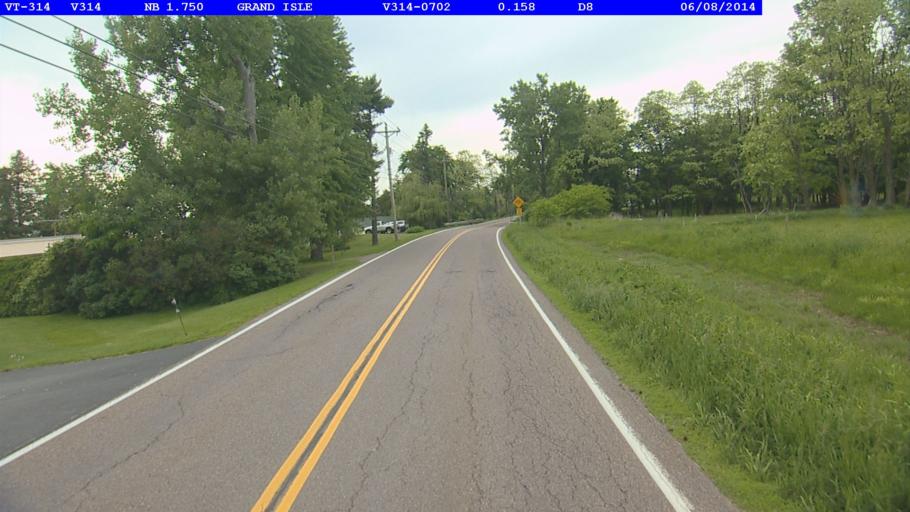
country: US
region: New York
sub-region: Clinton County
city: Cumberland Head
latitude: 44.6797
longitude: -73.3474
